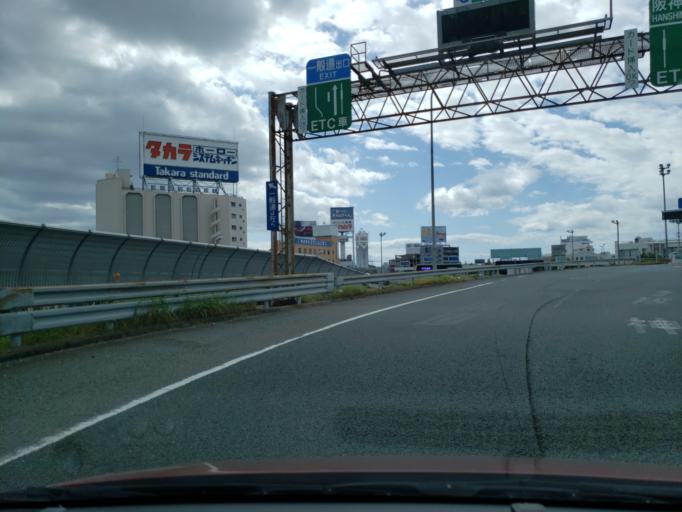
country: JP
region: Osaka
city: Toyonaka
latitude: 34.7510
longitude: 135.4647
